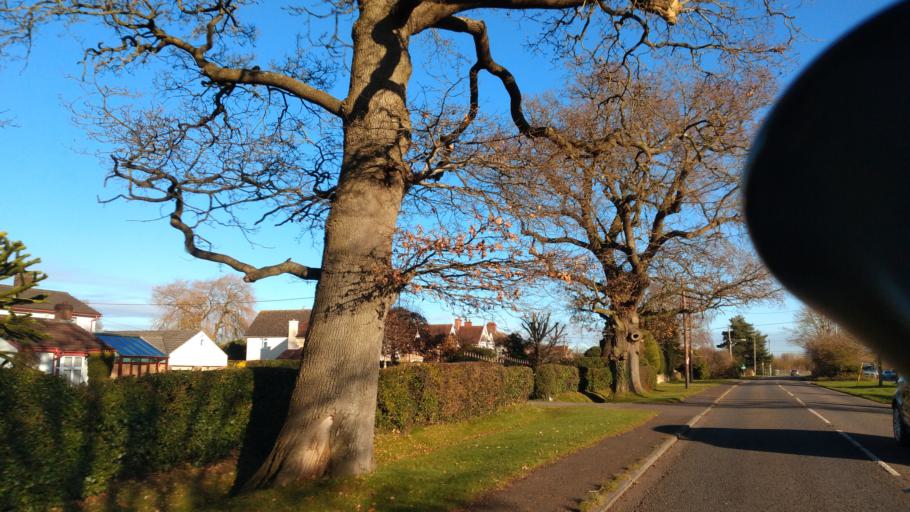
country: GB
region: England
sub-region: Somerset
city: Frome
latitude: 51.2300
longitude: -2.3018
